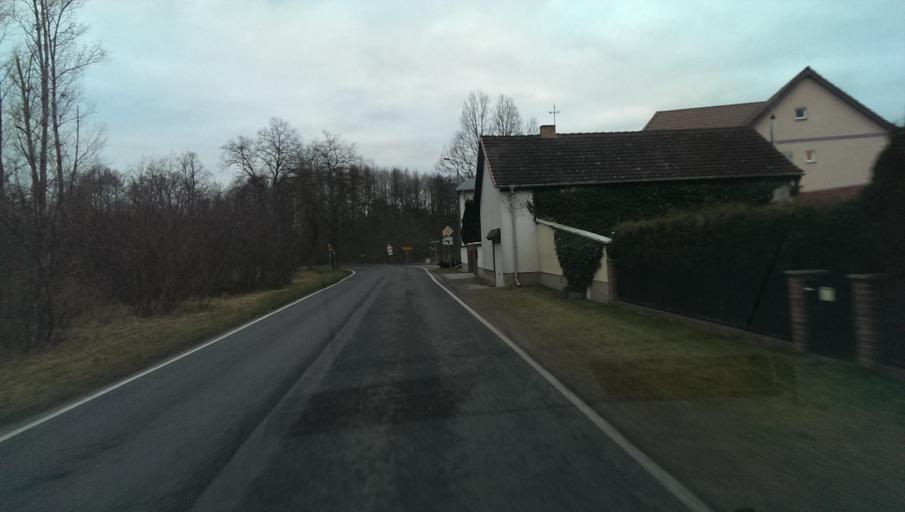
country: DE
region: Brandenburg
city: Sperenberg
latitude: 52.1578
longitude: 13.3454
